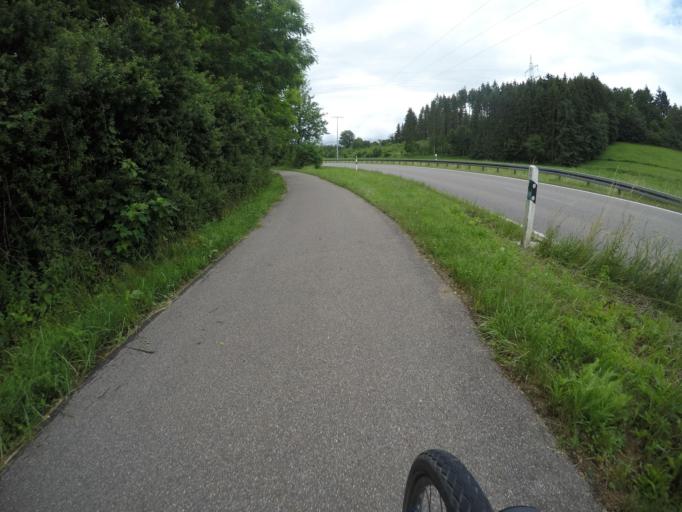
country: DE
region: Baden-Wuerttemberg
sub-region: Regierungsbezirk Stuttgart
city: Gartringen
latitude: 48.6532
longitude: 8.8824
